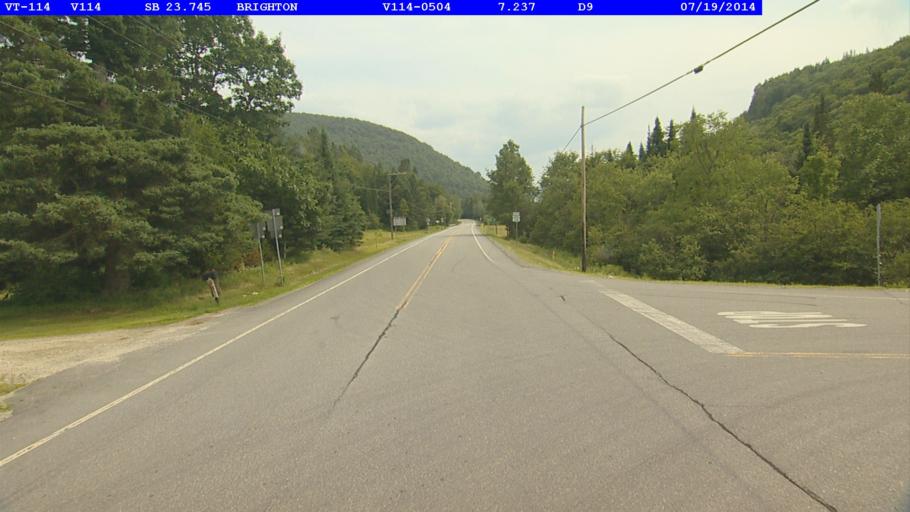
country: CA
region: Quebec
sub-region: Estrie
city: Coaticook
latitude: 44.8448
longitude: -71.9095
